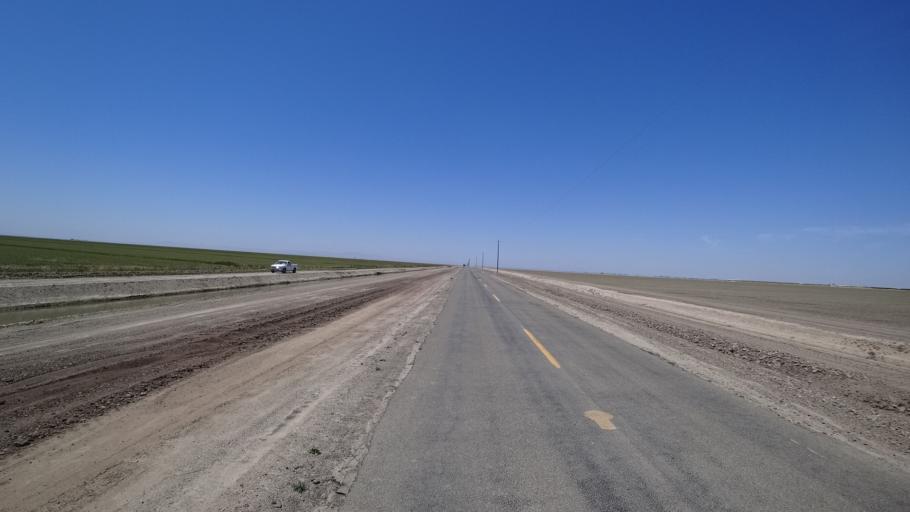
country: US
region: California
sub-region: Kings County
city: Corcoran
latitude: 36.1163
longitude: -119.6487
